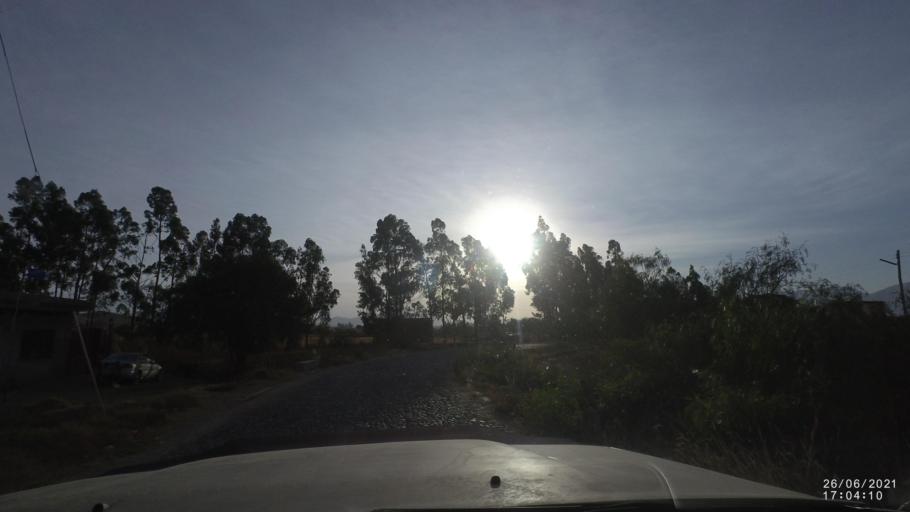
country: BO
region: Cochabamba
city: Cliza
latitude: -17.6374
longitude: -65.9152
